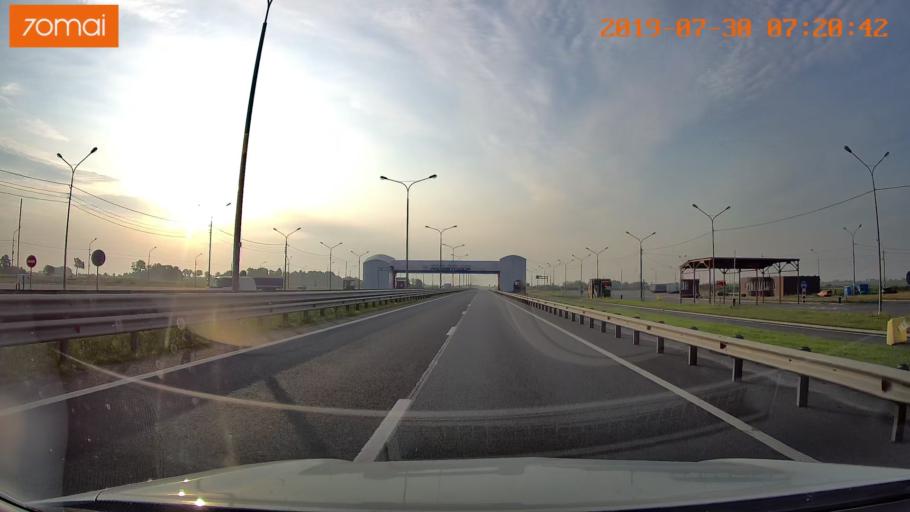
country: RU
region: Kaliningrad
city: Bol'shoe Isakovo
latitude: 54.6993
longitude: 20.7110
